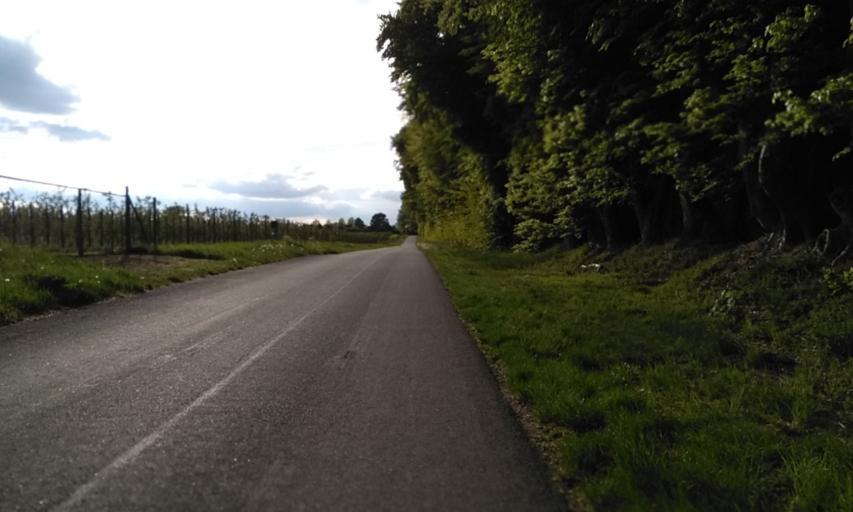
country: DE
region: Lower Saxony
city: Nottensdorf
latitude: 53.4806
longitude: 9.6100
